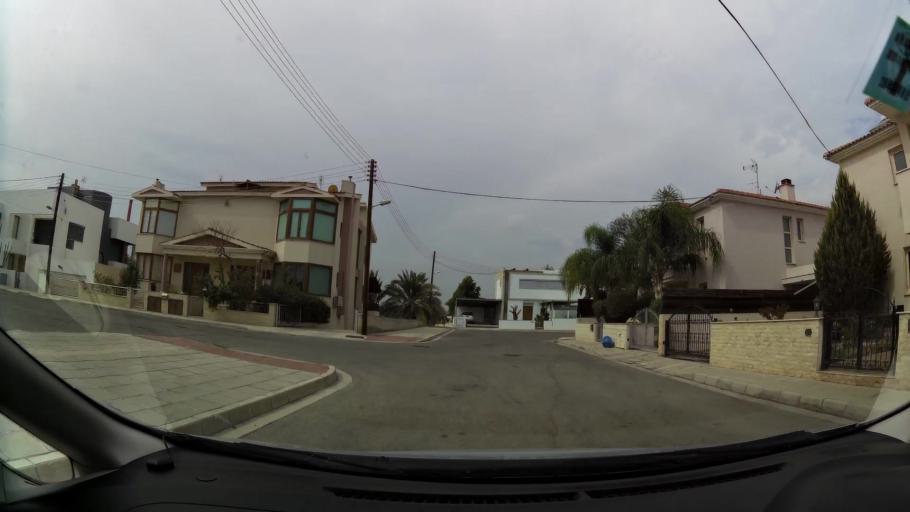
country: CY
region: Lefkosia
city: Geri
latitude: 35.0822
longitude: 33.3881
